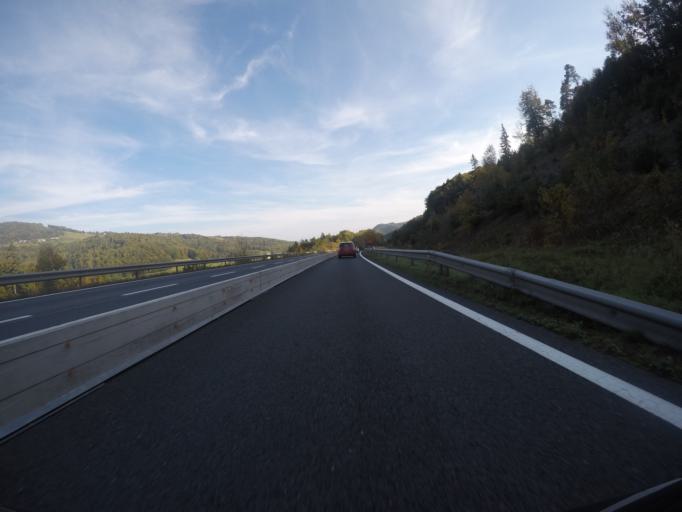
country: SI
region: Grosuplje
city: Grosuplje
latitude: 45.9710
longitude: 14.7214
